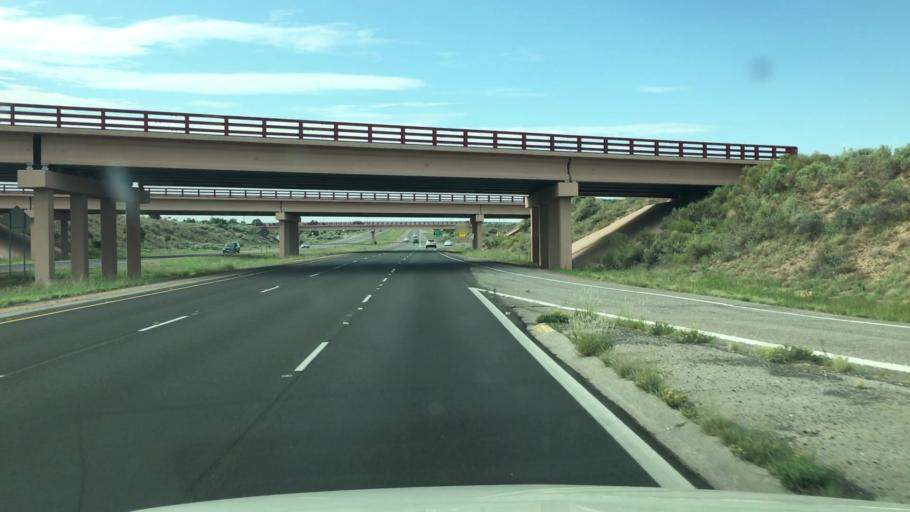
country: US
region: New Mexico
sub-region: Santa Fe County
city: Santa Fe
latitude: 35.6353
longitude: -105.9565
